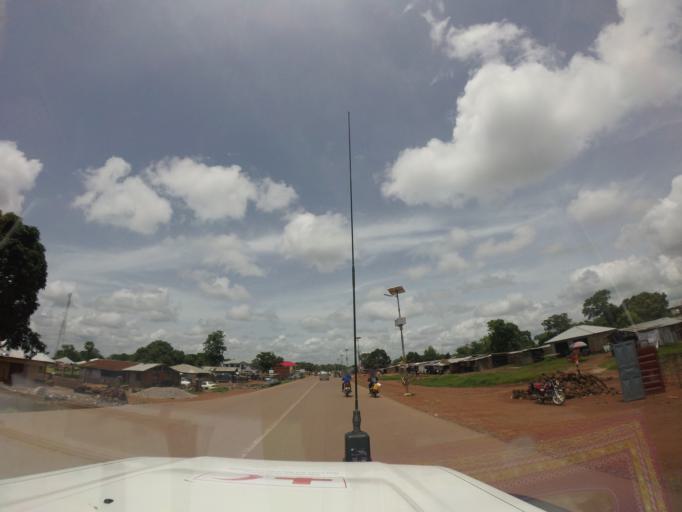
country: SL
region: Northern Province
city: Kambia
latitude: 9.1104
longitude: -12.9259
